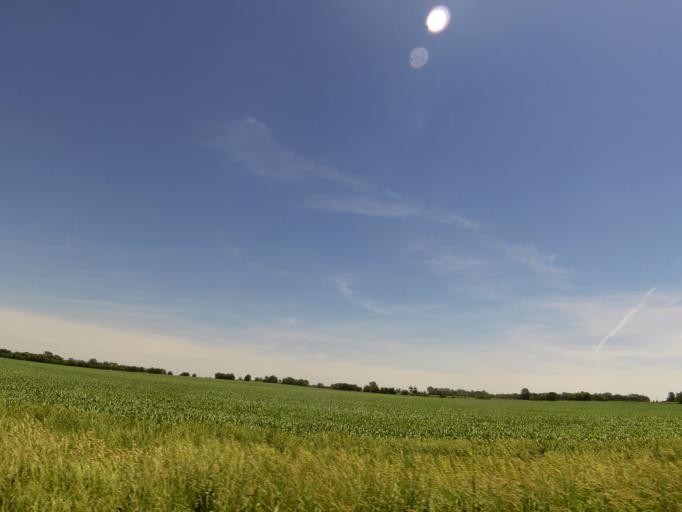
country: US
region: Illinois
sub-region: Vermilion County
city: Rossville
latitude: 40.3998
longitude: -87.6789
